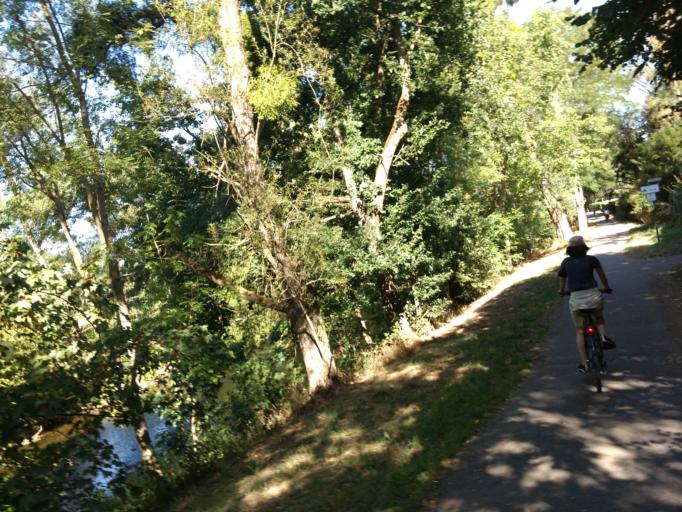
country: DE
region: Rheinland-Pfalz
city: Sinzig
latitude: 50.5484
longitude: 7.2339
